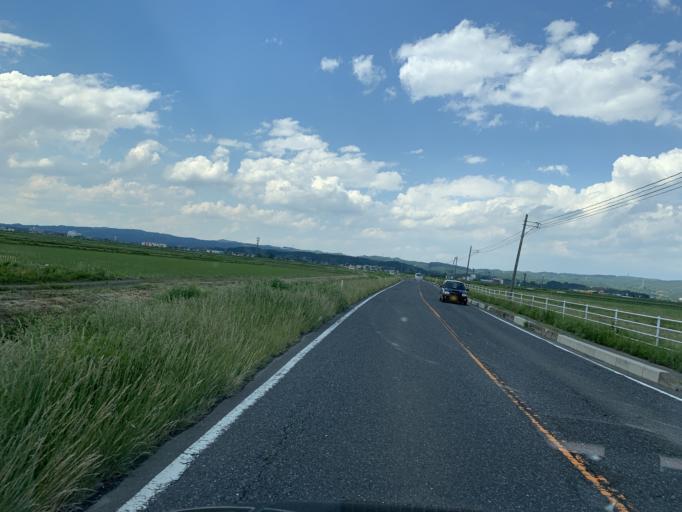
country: JP
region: Miyagi
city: Wakuya
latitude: 38.5223
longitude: 141.1298
